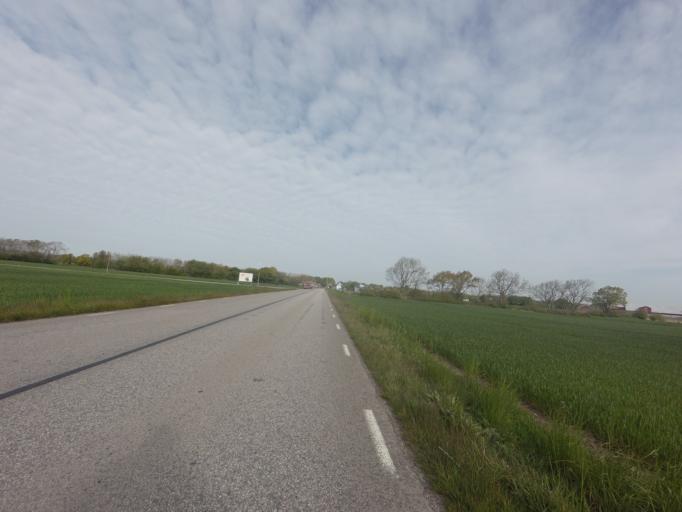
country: SE
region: Skane
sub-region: Hoganas Kommun
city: Hoganas
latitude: 56.1873
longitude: 12.5879
